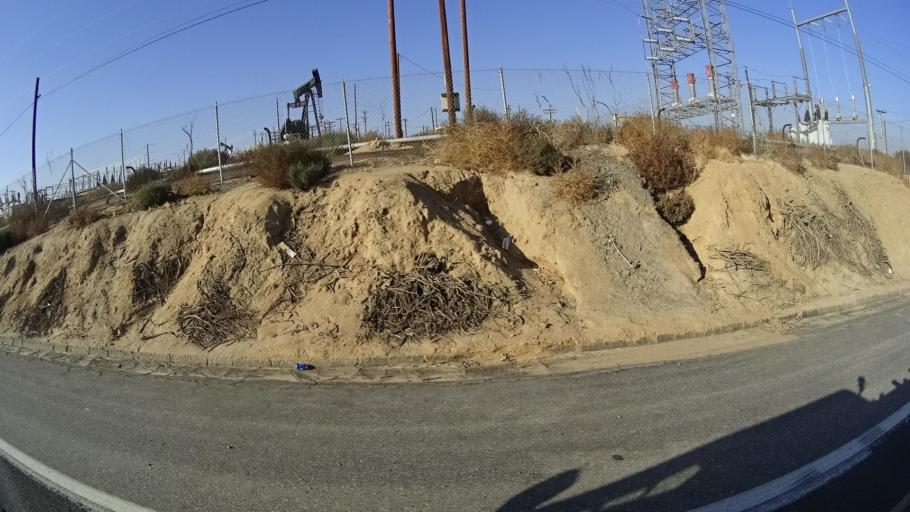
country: US
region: California
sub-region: Kern County
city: Oildale
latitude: 35.4277
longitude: -118.9765
